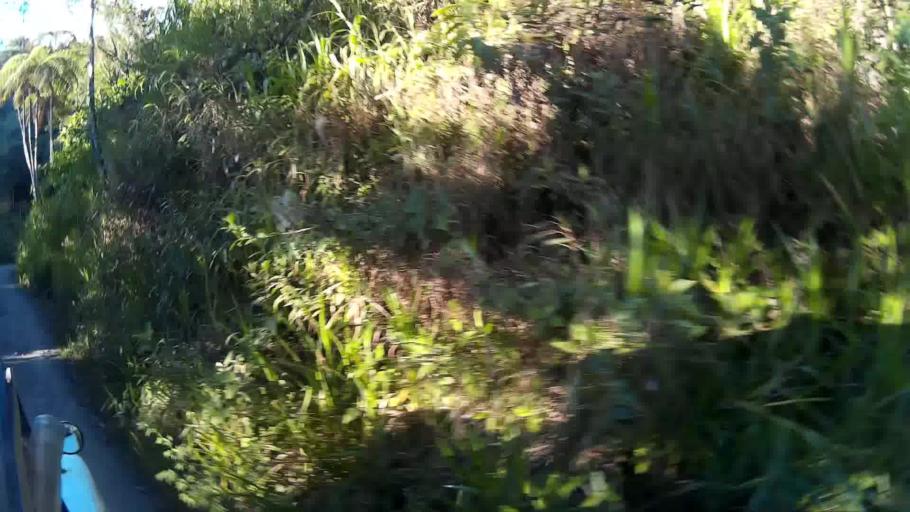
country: CO
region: Quindio
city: Filandia
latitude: 4.7263
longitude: -75.6827
